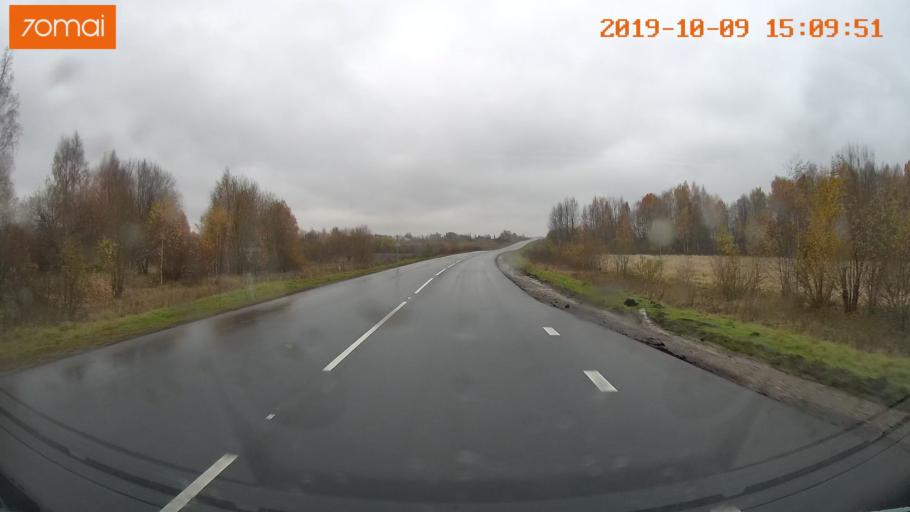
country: RU
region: Kostroma
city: Susanino
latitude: 58.1856
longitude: 41.6480
